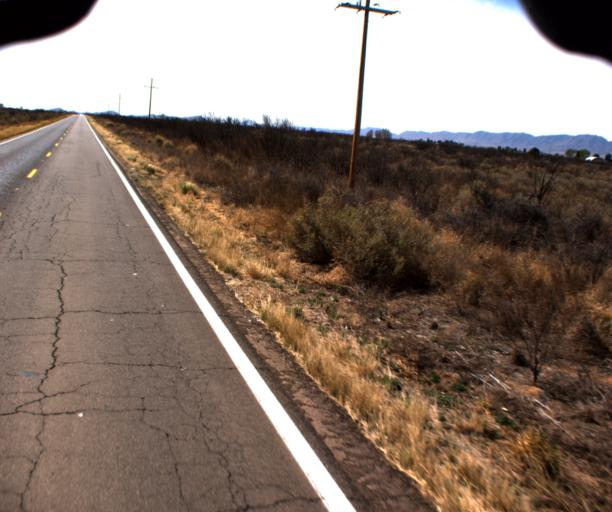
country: US
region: Arizona
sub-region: Cochise County
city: Willcox
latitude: 32.0036
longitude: -109.8628
